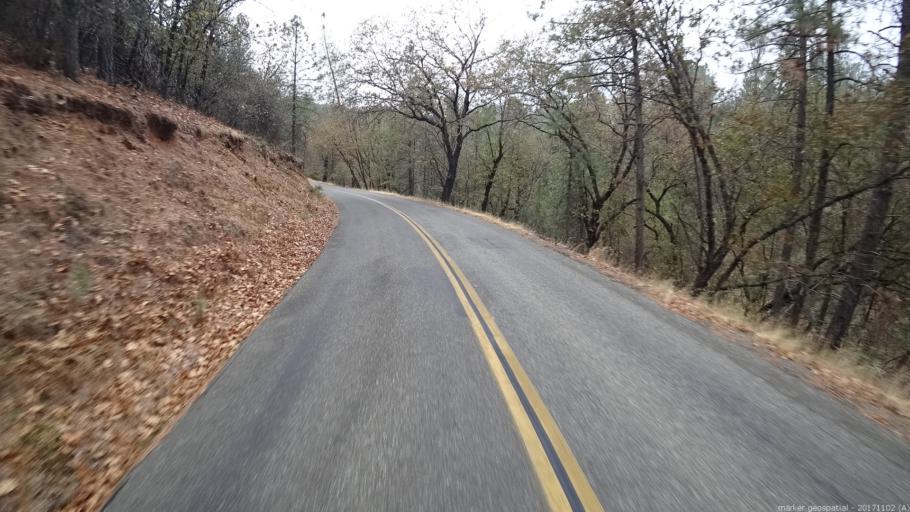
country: US
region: California
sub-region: Shasta County
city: Bella Vista
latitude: 40.7439
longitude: -122.2406
